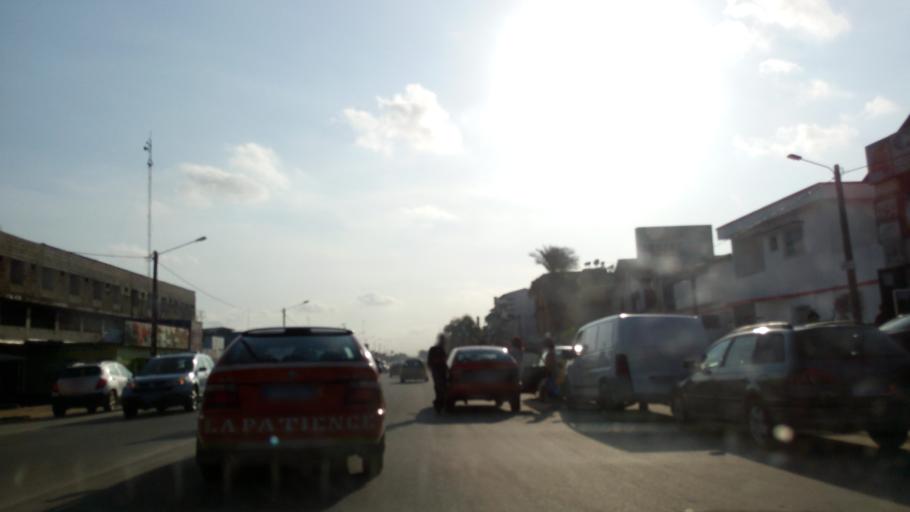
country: CI
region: Lagunes
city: Abobo
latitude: 5.4030
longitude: -3.9791
